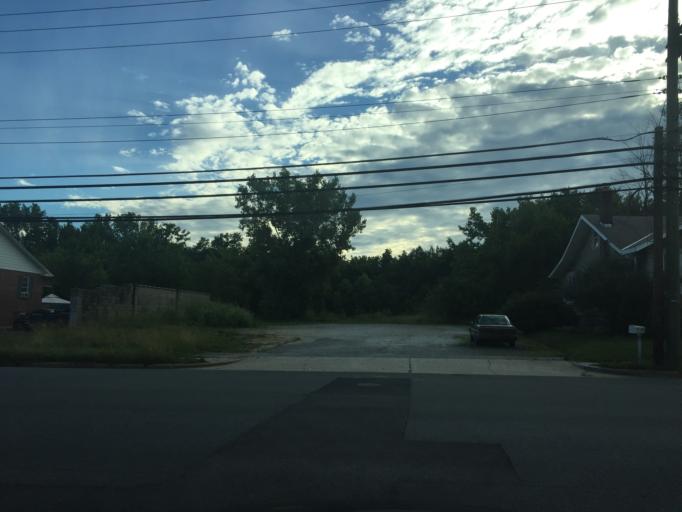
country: US
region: Maryland
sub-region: Baltimore County
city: Middle River
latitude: 39.3392
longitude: -76.4477
